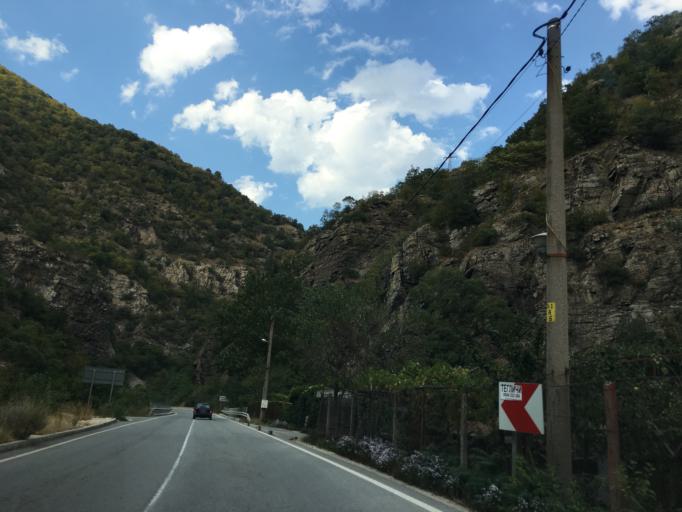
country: BG
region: Pazardzhik
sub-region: Obshtina Septemvri
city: Septemvri
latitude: 42.1357
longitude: 24.1253
